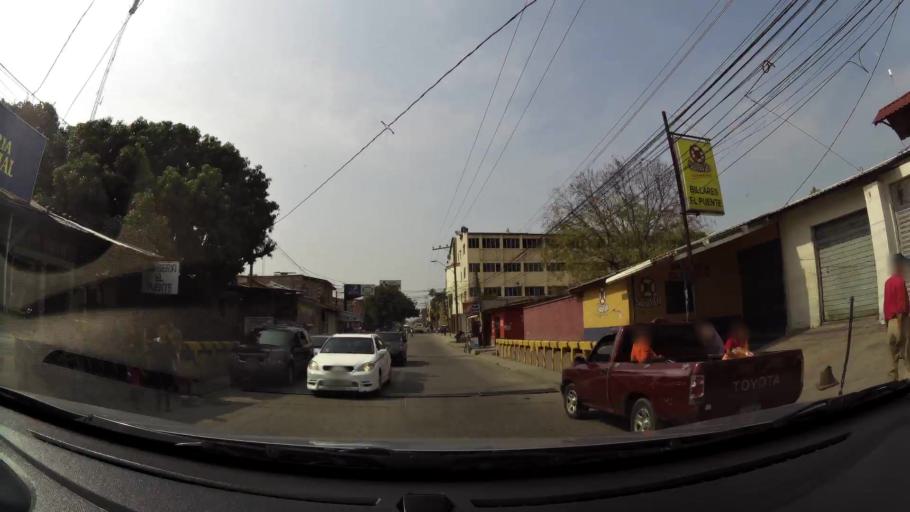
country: HN
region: Comayagua
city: Comayagua
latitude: 14.4545
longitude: -87.6392
